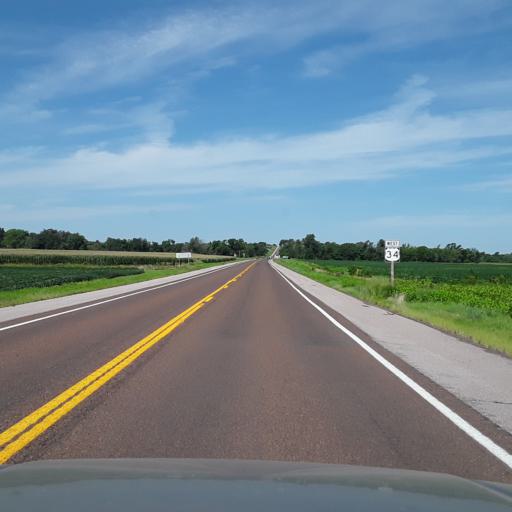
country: US
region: Nebraska
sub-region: Lancaster County
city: Lincoln
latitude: 40.8865
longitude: -96.8282
